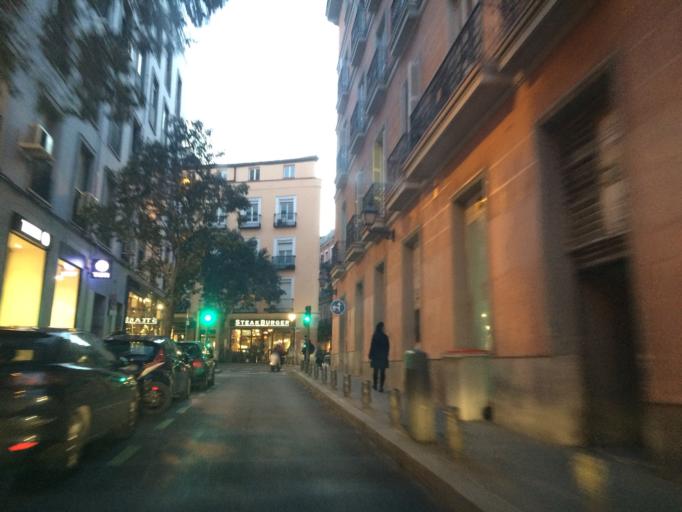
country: ES
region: Madrid
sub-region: Provincia de Madrid
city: City Center
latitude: 40.4251
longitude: -3.7003
